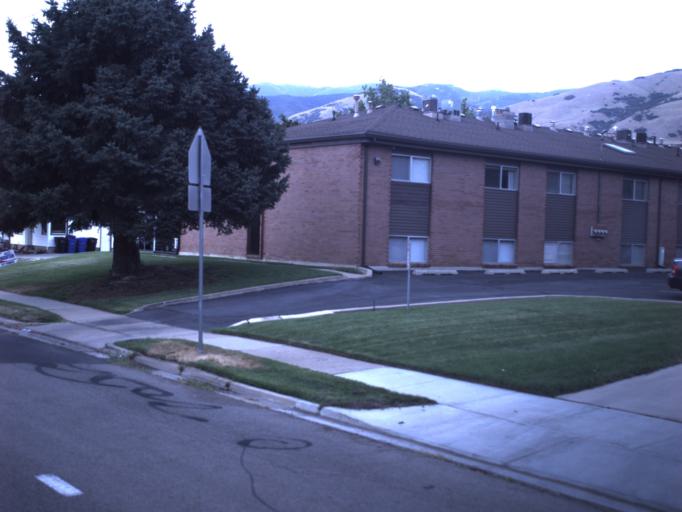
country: US
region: Utah
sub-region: Davis County
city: Bountiful
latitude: 40.8949
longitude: -111.8790
